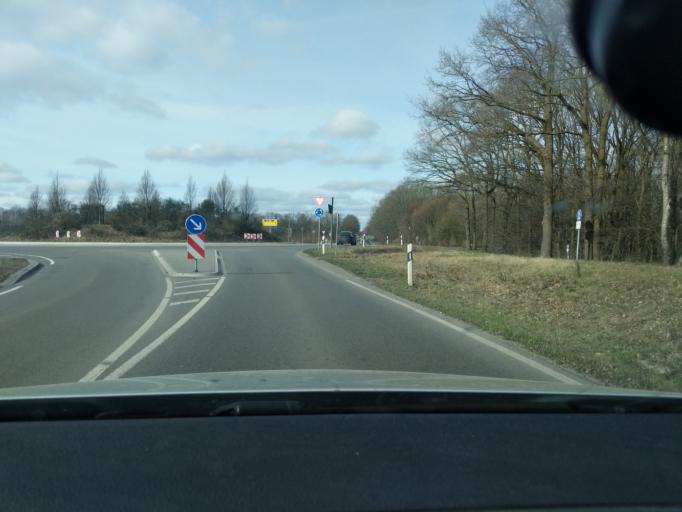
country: DE
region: Lower Saxony
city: Agathenburg
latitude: 53.5700
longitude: 9.5196
